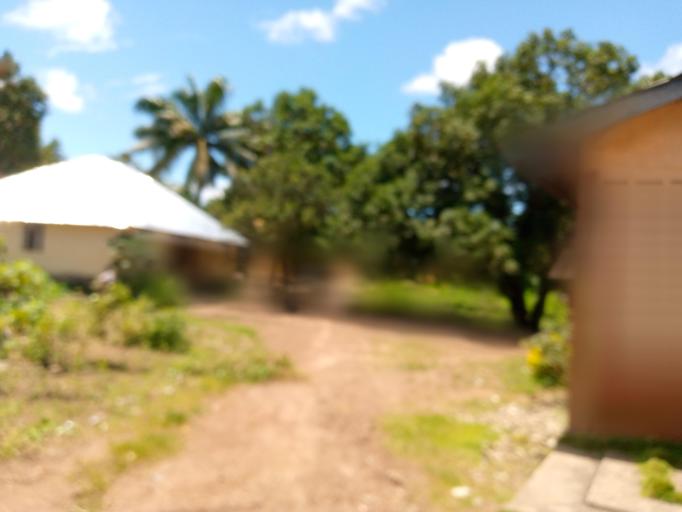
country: SL
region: Northern Province
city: Makeni
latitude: 9.0333
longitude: -12.1620
